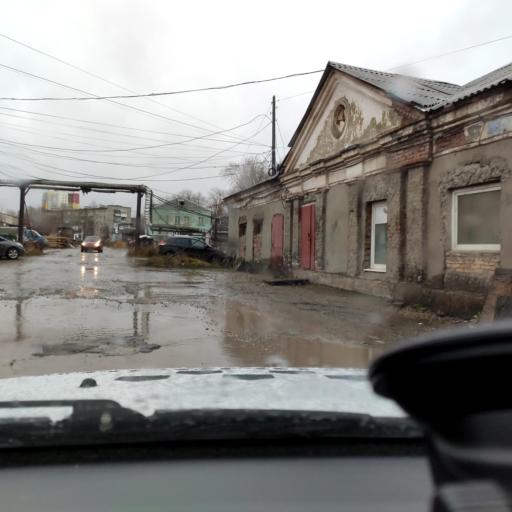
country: RU
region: Perm
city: Perm
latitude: 57.9755
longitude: 56.2811
